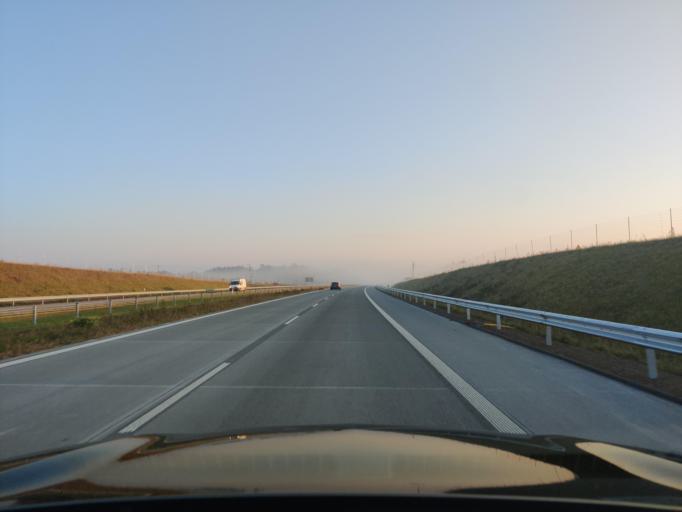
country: PL
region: Masovian Voivodeship
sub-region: Powiat mlawski
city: Mlawa
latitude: 53.1252
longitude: 20.4125
